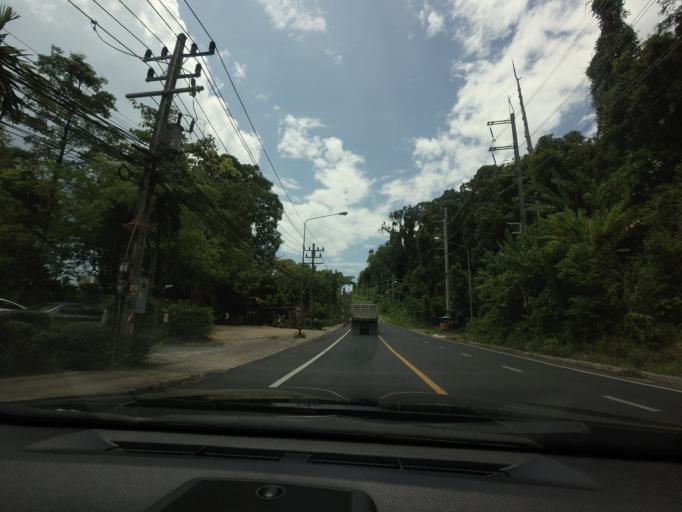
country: TH
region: Phangnga
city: Ban Khao Lak
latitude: 8.6317
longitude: 98.2465
